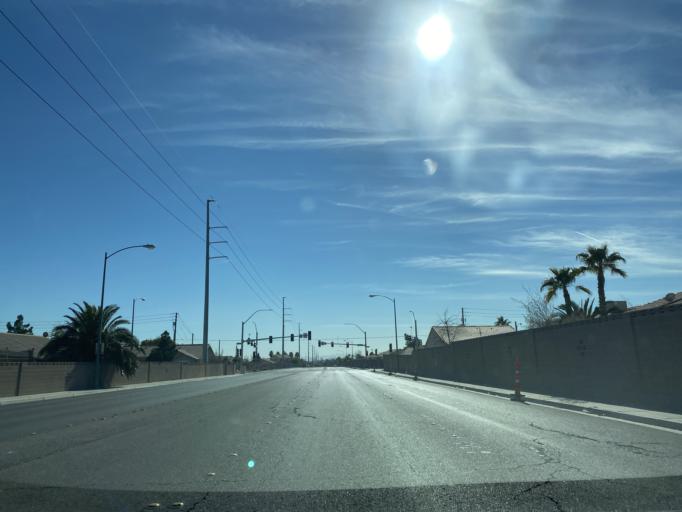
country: US
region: Nevada
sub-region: Clark County
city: North Las Vegas
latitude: 36.2552
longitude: -115.1441
